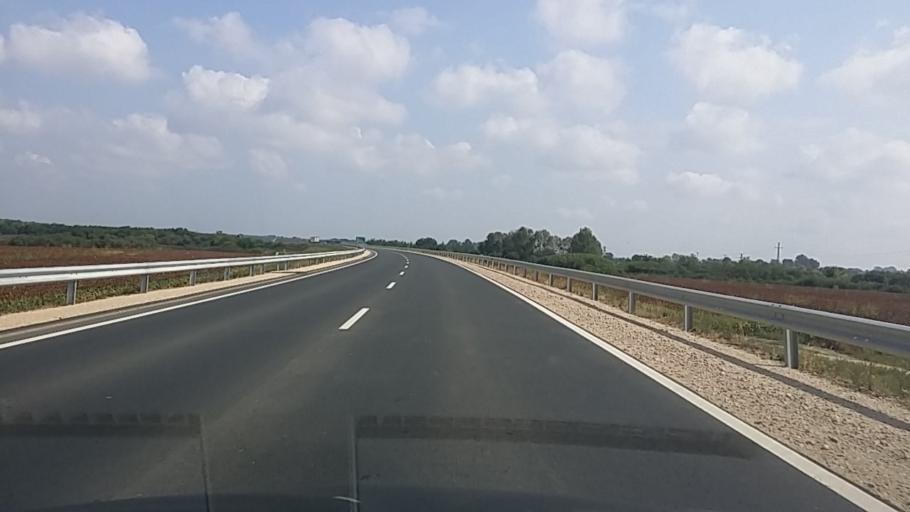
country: HU
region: Csongrad
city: Hodmezovasarhely
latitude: 46.4401
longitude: 20.3041
